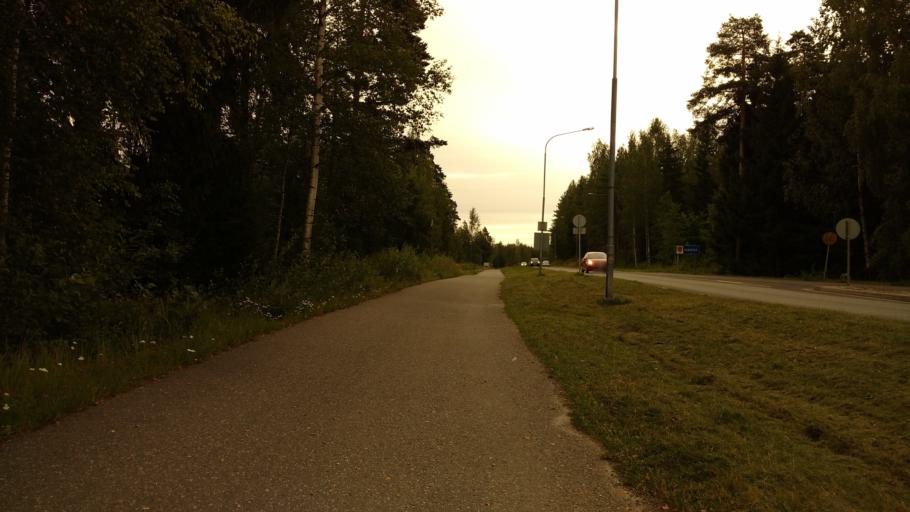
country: FI
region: Varsinais-Suomi
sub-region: Turku
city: Kaarina
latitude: 60.4433
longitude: 22.3657
